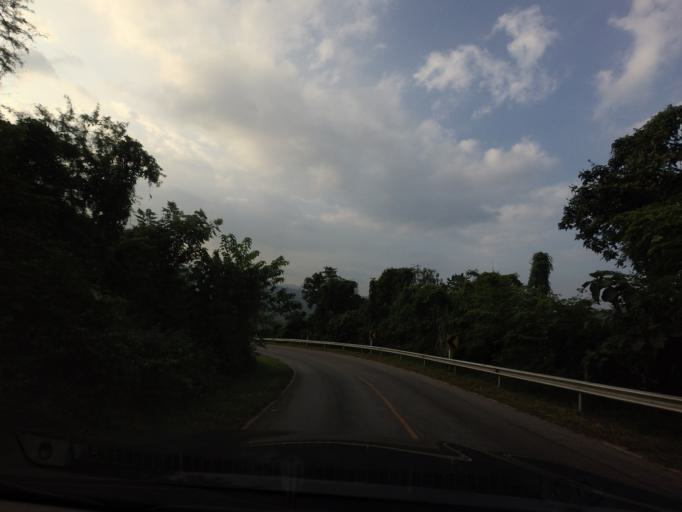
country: TH
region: Loei
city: Na Haeo
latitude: 17.3678
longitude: 101.0499
